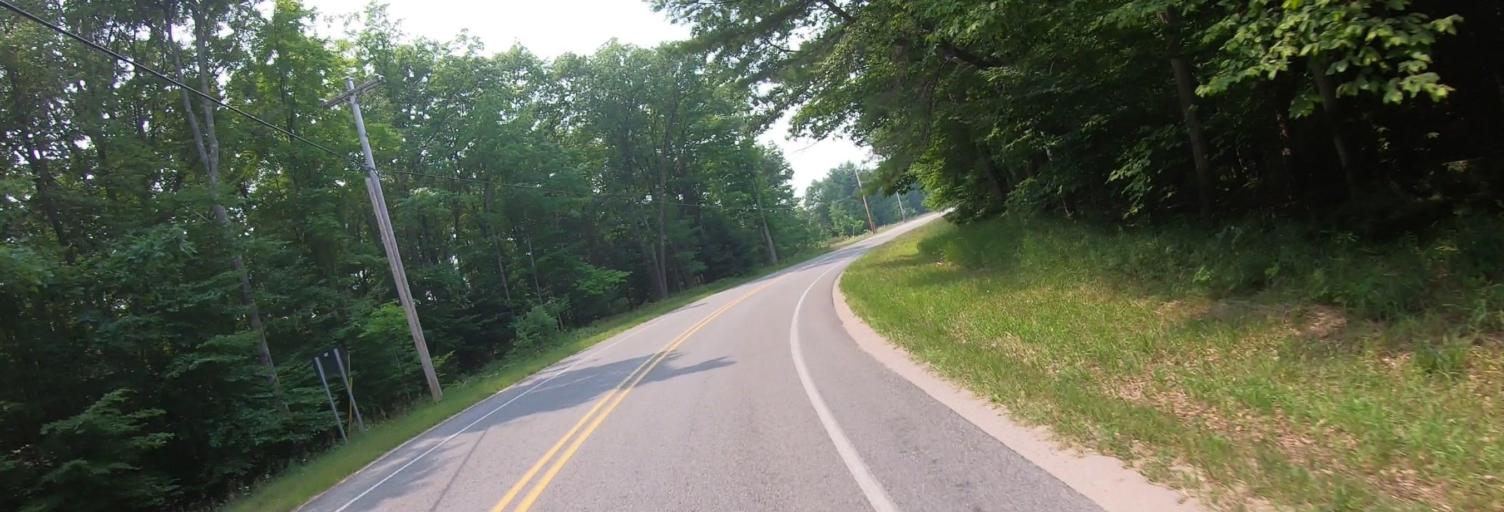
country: US
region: Michigan
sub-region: Leelanau County
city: Leland
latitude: 45.1756
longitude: -85.5414
